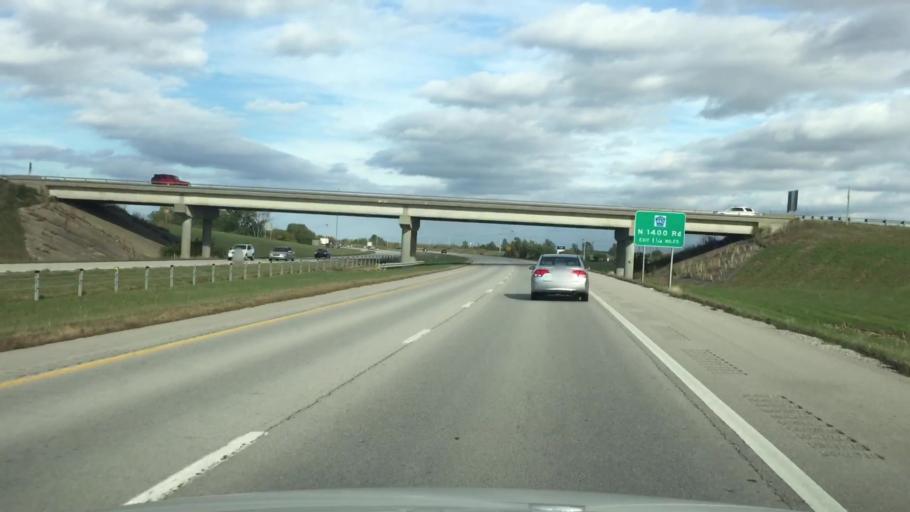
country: US
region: Kansas
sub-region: Douglas County
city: Eudora
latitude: 38.9314
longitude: -95.0988
